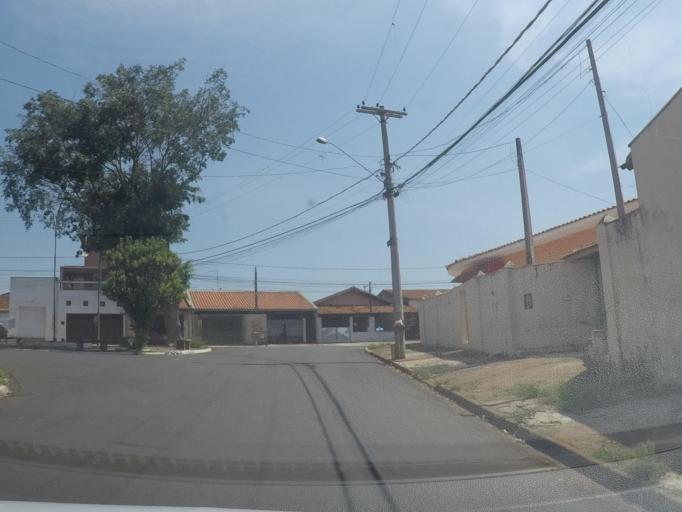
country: BR
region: Sao Paulo
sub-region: Sumare
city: Sumare
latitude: -22.8401
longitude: -47.2699
